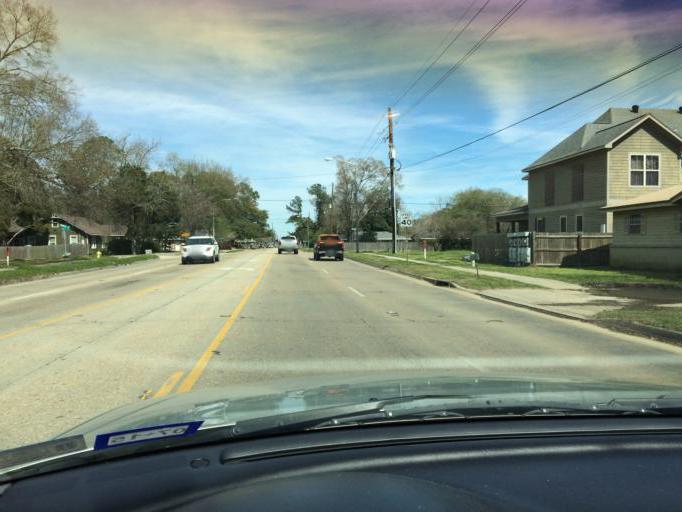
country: US
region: Louisiana
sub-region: Lafayette Parish
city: Scott
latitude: 30.2035
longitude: -92.0623
